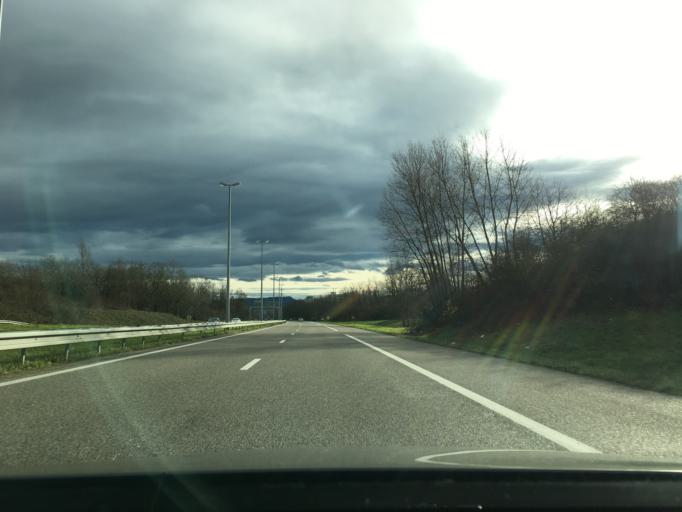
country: FR
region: Alsace
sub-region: Departement du Haut-Rhin
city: Saint-Louis
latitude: 47.5879
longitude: 7.5475
